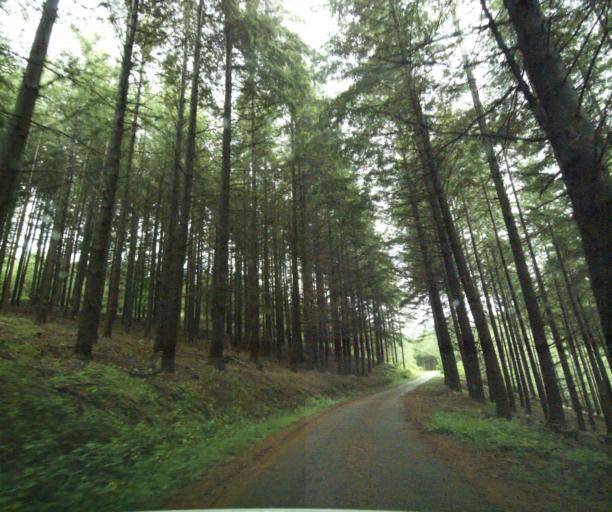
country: FR
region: Bourgogne
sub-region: Departement de Saone-et-Loire
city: Matour
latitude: 46.4481
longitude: 4.4680
